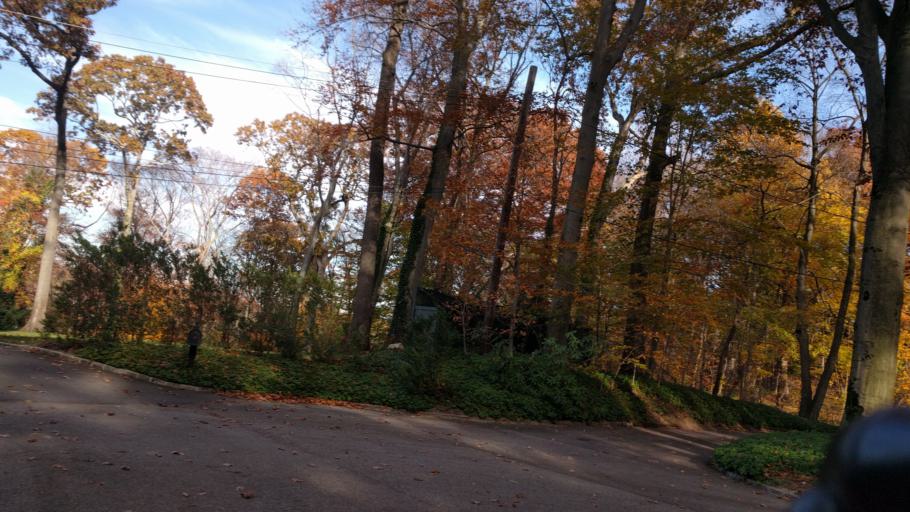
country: US
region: New York
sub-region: Nassau County
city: Locust Valley
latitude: 40.8754
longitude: -73.5817
